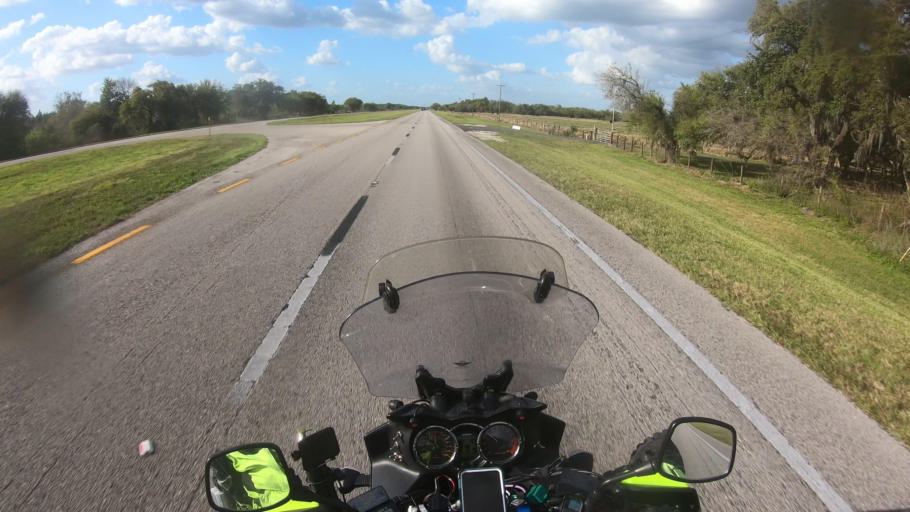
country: US
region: Florida
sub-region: Hendry County
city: Port LaBelle
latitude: 26.9983
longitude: -81.3284
